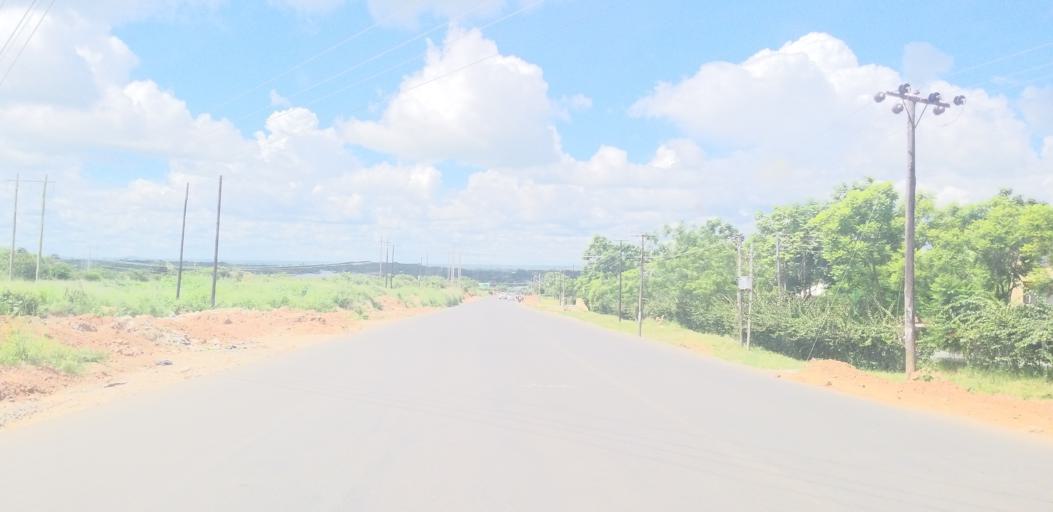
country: ZM
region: Lusaka
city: Lusaka
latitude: -15.3476
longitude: 28.3265
